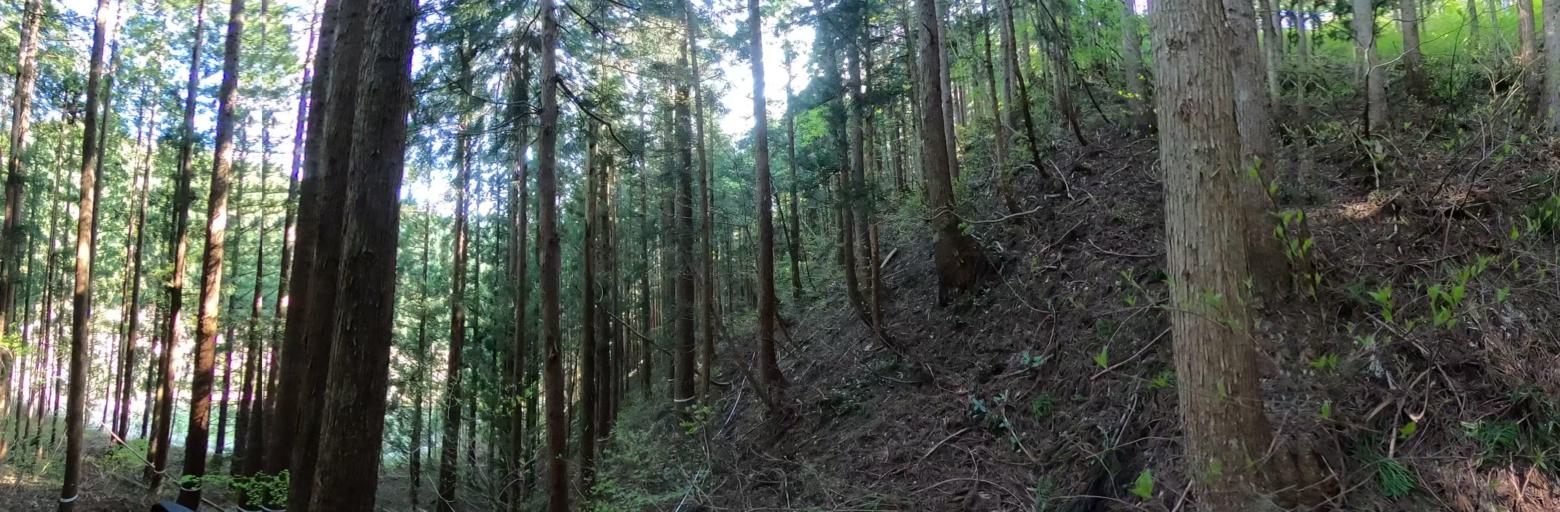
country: JP
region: Yamagata
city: Shinjo
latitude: 38.8882
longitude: 140.4071
